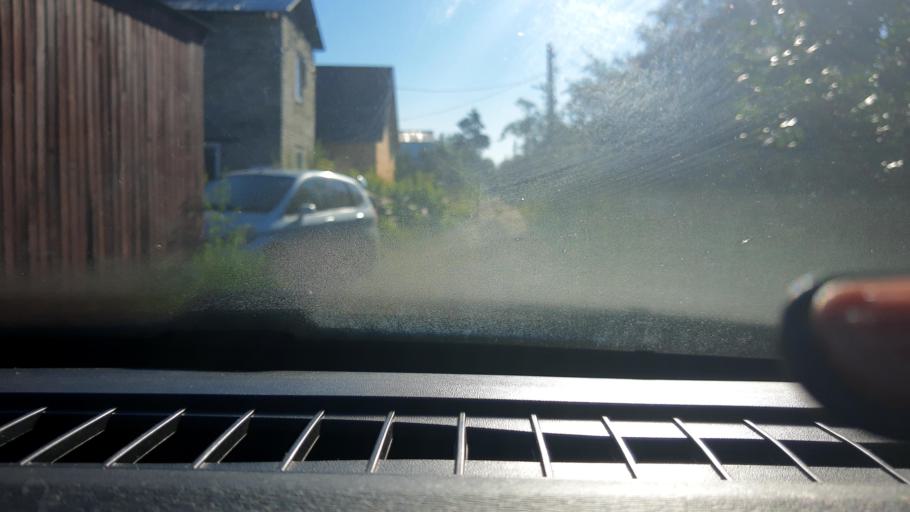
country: RU
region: Nizjnij Novgorod
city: Gorbatovka
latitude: 56.3147
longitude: 43.8272
